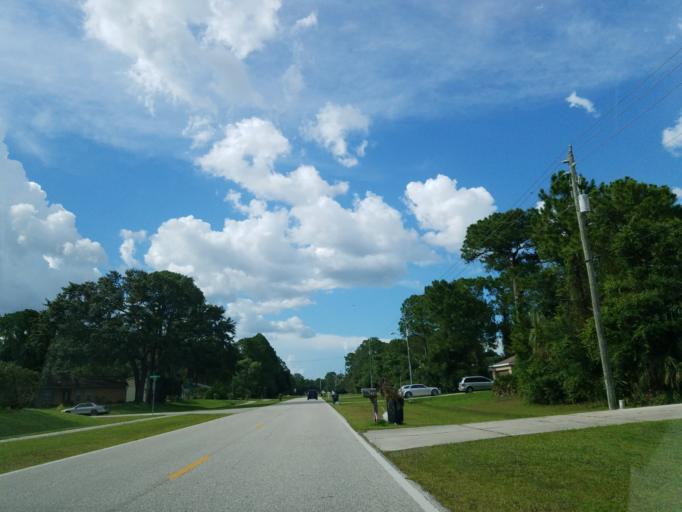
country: US
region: Florida
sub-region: Sarasota County
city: North Port
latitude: 27.0782
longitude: -82.1839
